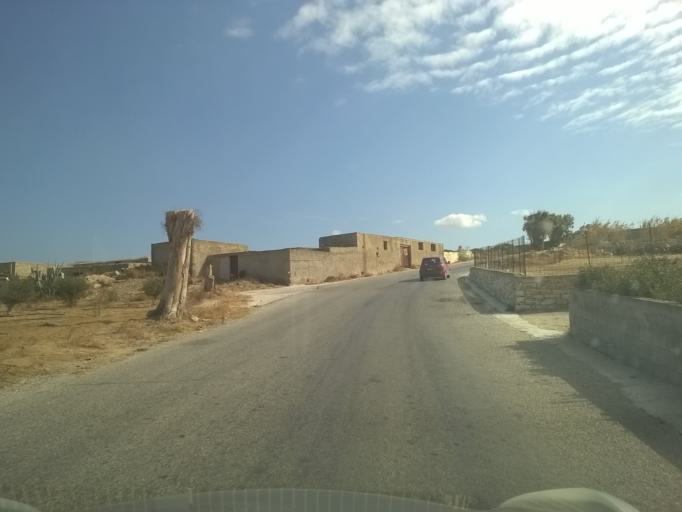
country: GR
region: South Aegean
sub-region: Nomos Kykladon
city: Naxos
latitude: 37.0662
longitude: 25.3911
